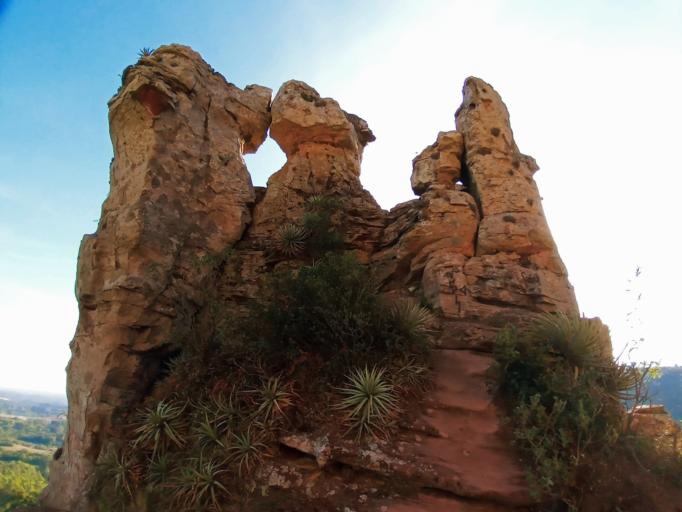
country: BR
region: Rio Grande do Sul
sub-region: Gravatai
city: Gravatai
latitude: -29.8615
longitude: -50.9833
